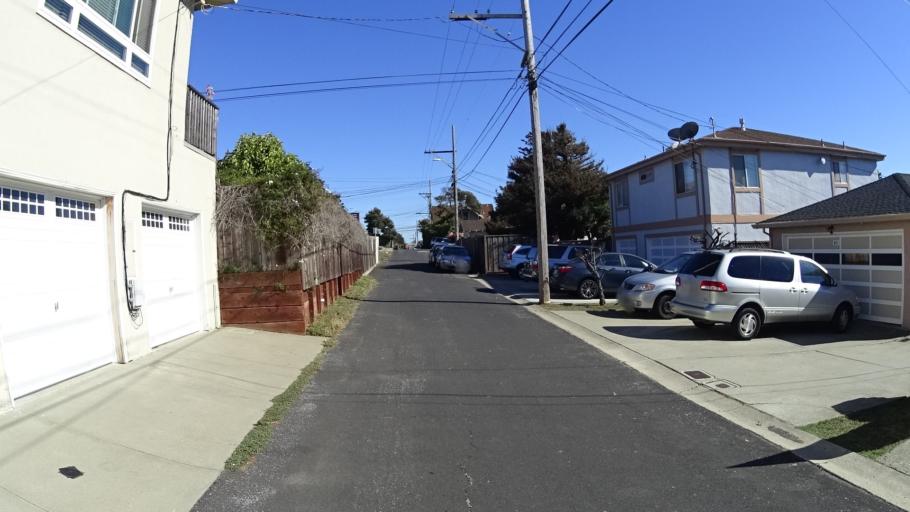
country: US
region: California
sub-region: San Mateo County
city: South San Francisco
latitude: 37.6586
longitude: -122.4279
